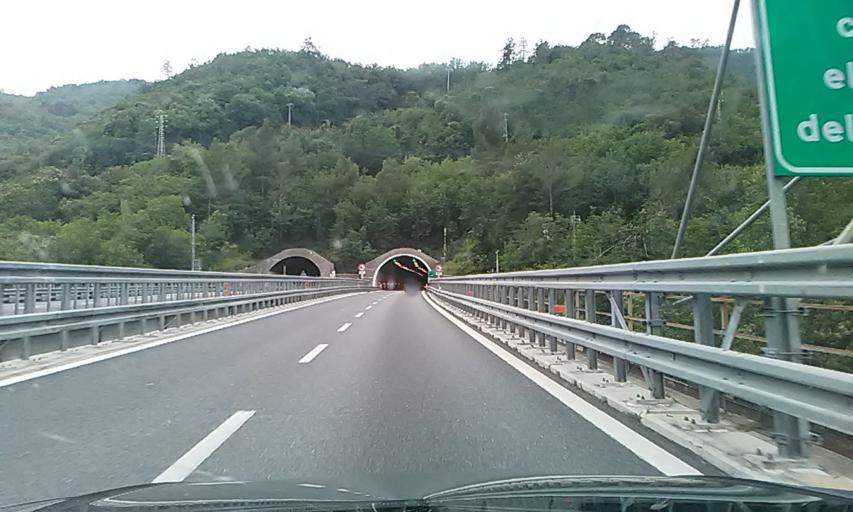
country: IT
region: Liguria
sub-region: Provincia di Savona
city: Villafranca
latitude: 44.0193
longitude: 8.1316
